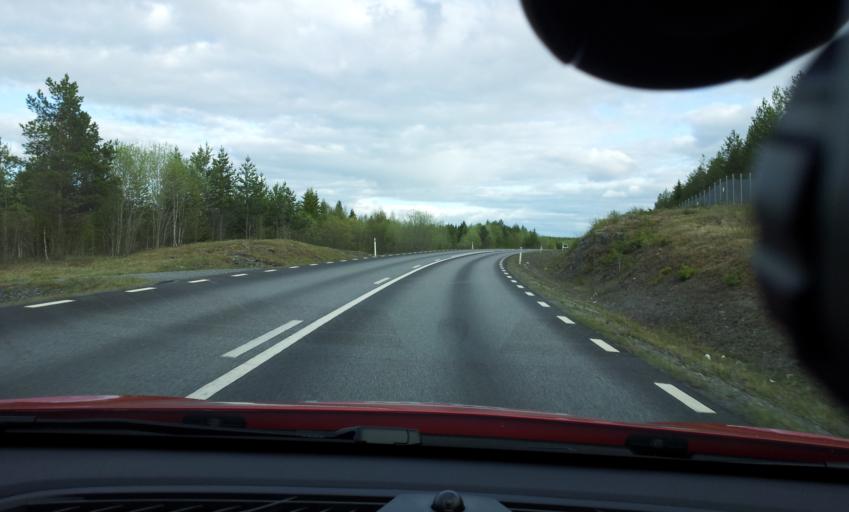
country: SE
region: Jaemtland
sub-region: OEstersunds Kommun
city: Ostersund
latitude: 63.1934
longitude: 14.5250
